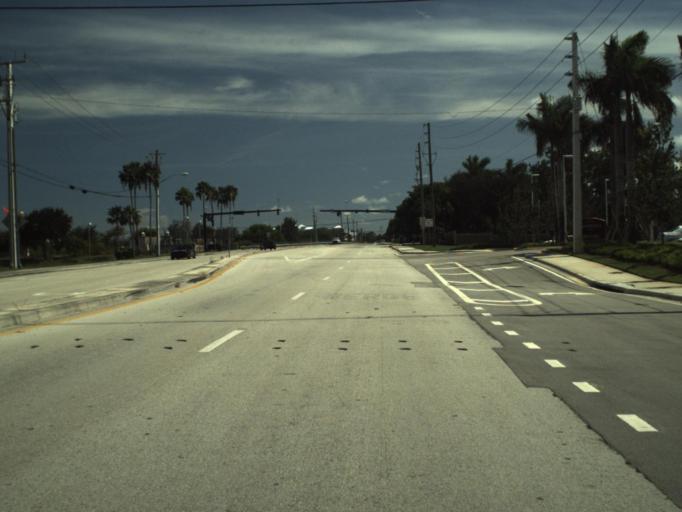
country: US
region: Florida
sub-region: Broward County
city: Dania Beach
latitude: 26.0620
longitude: -80.1686
